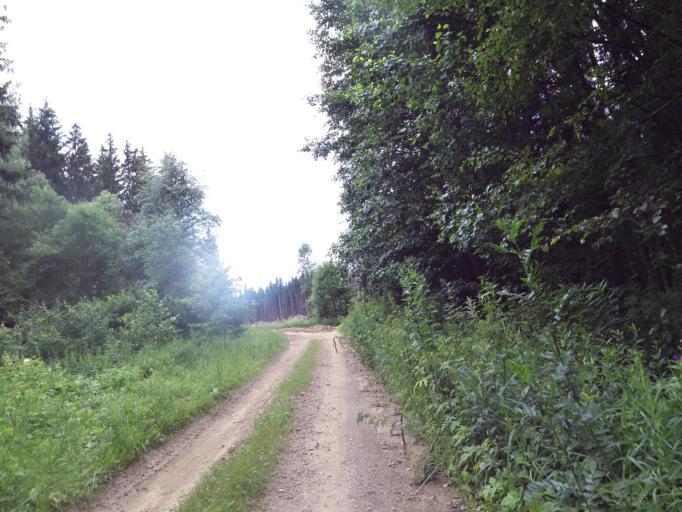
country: RU
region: Moskovskaya
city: Danki
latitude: 54.9432
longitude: 37.6857
